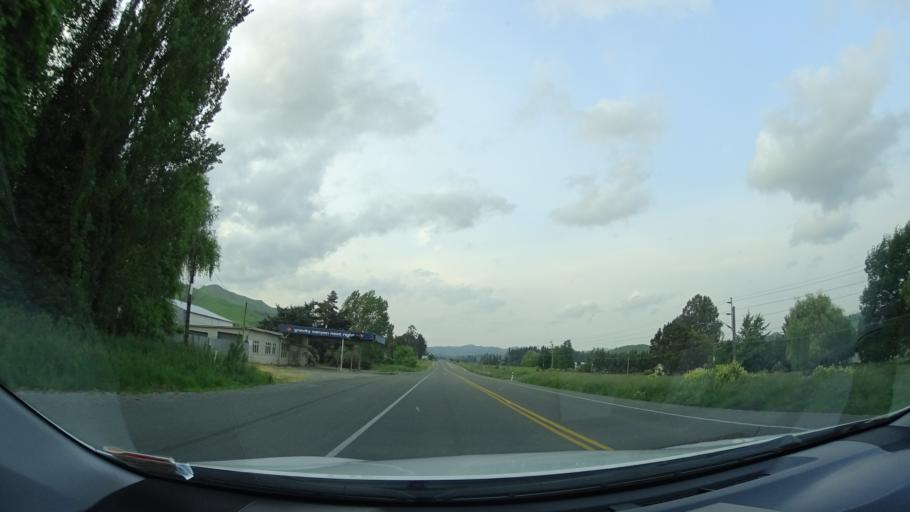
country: NZ
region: Manawatu-Wanganui
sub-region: Ruapehu District
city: Waiouru
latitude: -39.7303
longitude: 175.8436
